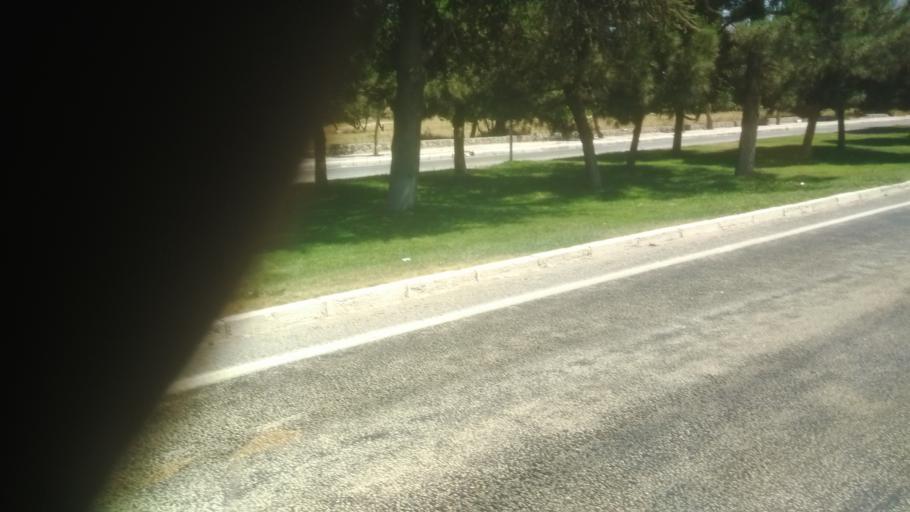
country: TR
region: Isparta
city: Isparta
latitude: 37.7819
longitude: 30.5664
